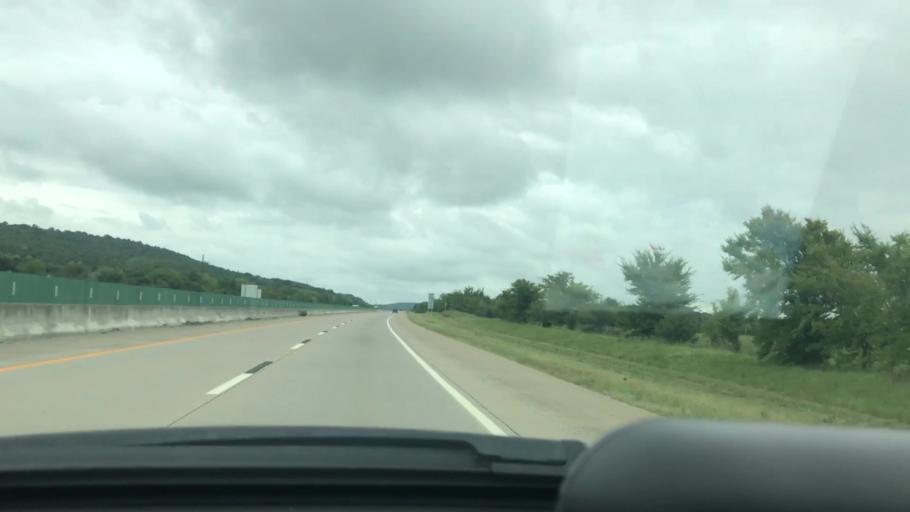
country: US
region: Oklahoma
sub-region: Pittsburg County
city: Krebs
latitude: 35.0660
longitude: -95.7057
